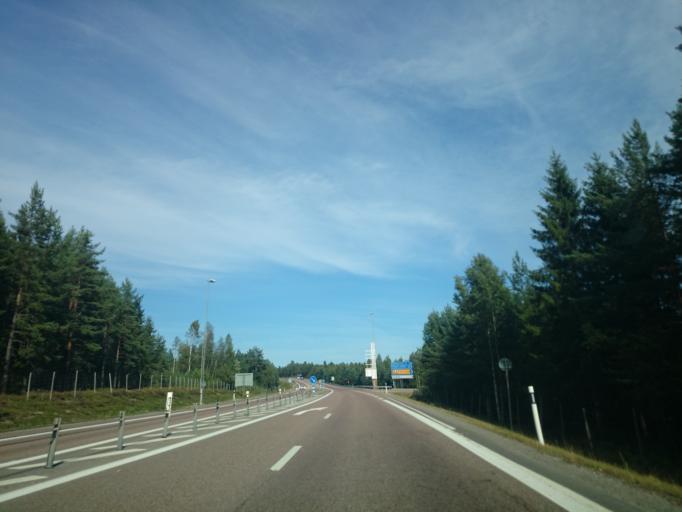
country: SE
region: Gaevleborg
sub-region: Hudiksvalls Kommun
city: Hudiksvall
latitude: 61.7765
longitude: 17.1183
